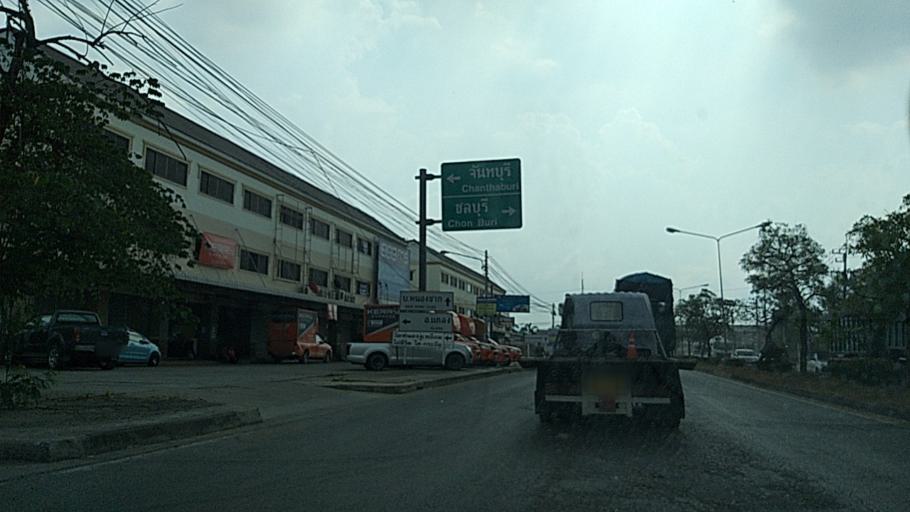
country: TH
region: Chon Buri
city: Ban Bueng
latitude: 13.2914
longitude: 101.1748
